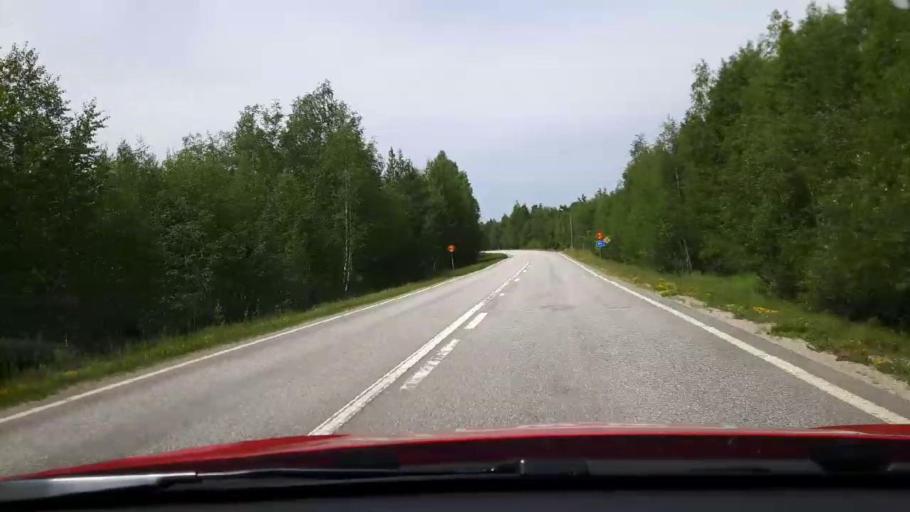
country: SE
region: Jaemtland
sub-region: Harjedalens Kommun
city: Sveg
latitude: 62.1270
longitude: 14.0677
